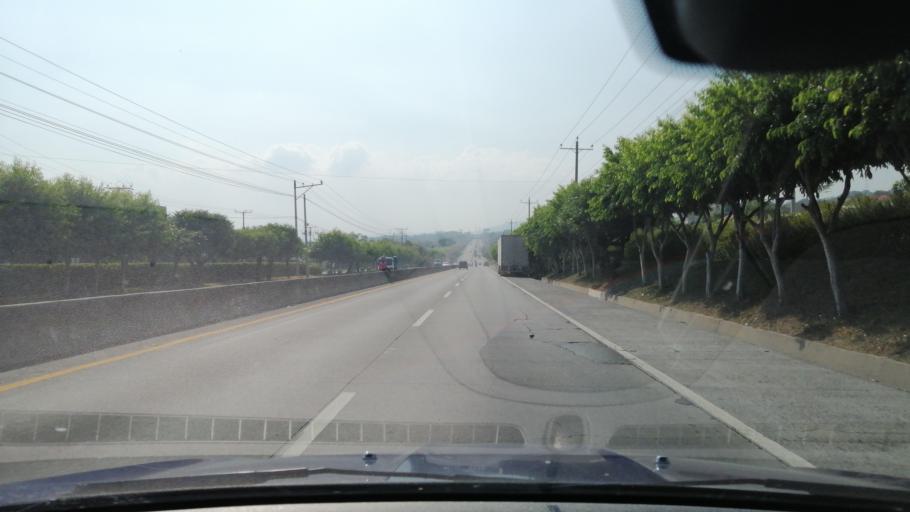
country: SV
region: San Salvador
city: Apopa
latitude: 13.7950
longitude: -89.2265
